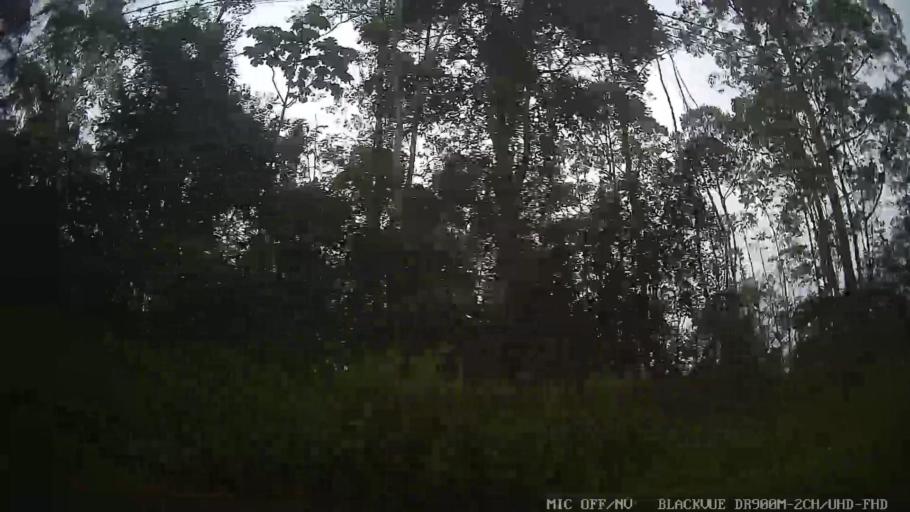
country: BR
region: Sao Paulo
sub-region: Suzano
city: Suzano
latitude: -23.6671
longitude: -46.2372
